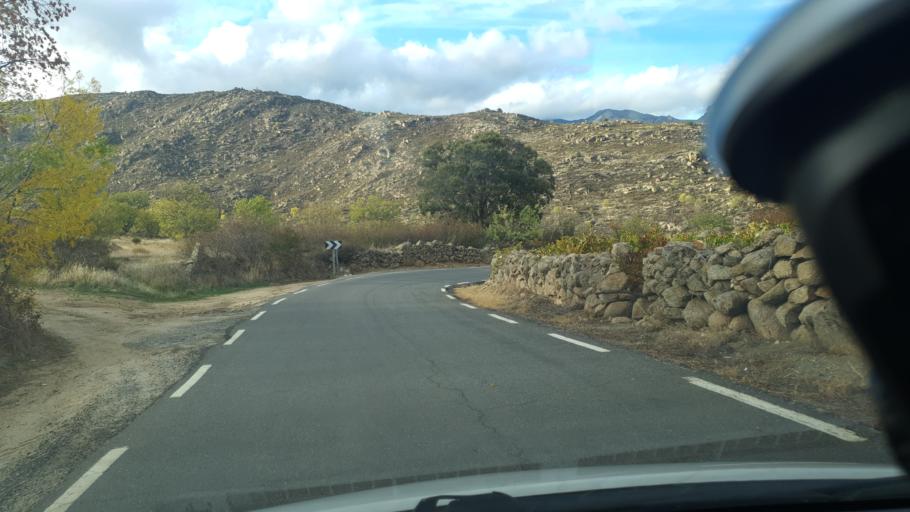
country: ES
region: Castille and Leon
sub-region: Provincia de Avila
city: Burgohondo
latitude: 40.4108
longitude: -4.8128
